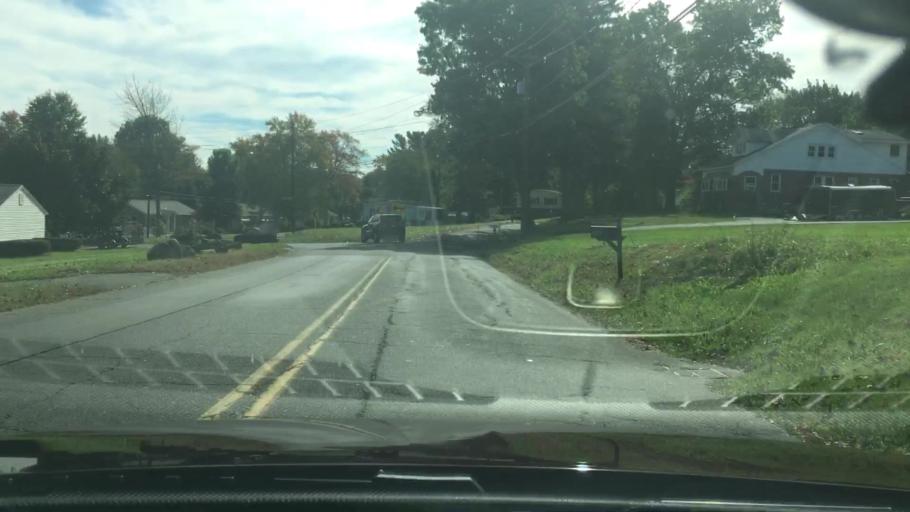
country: US
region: Connecticut
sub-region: Hartford County
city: Plainville
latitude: 41.6502
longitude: -72.8831
